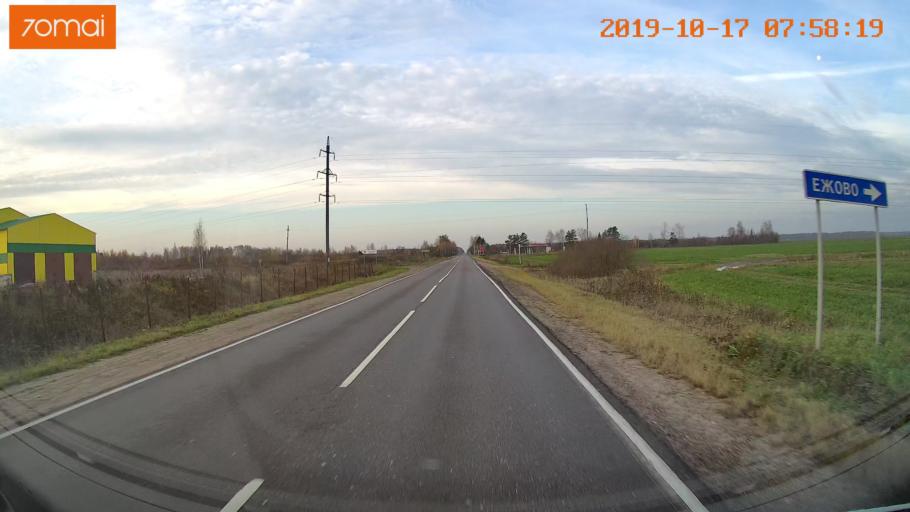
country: RU
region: Vladimir
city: Bavleny
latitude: 56.4037
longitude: 39.5598
